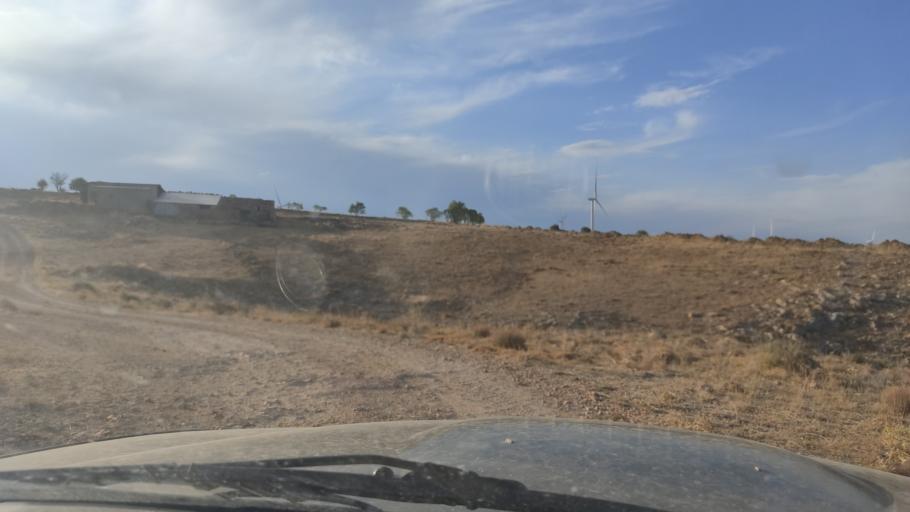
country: ES
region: Aragon
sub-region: Provincia de Teruel
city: Monforte de Moyuela
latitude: 41.0655
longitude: -0.9923
